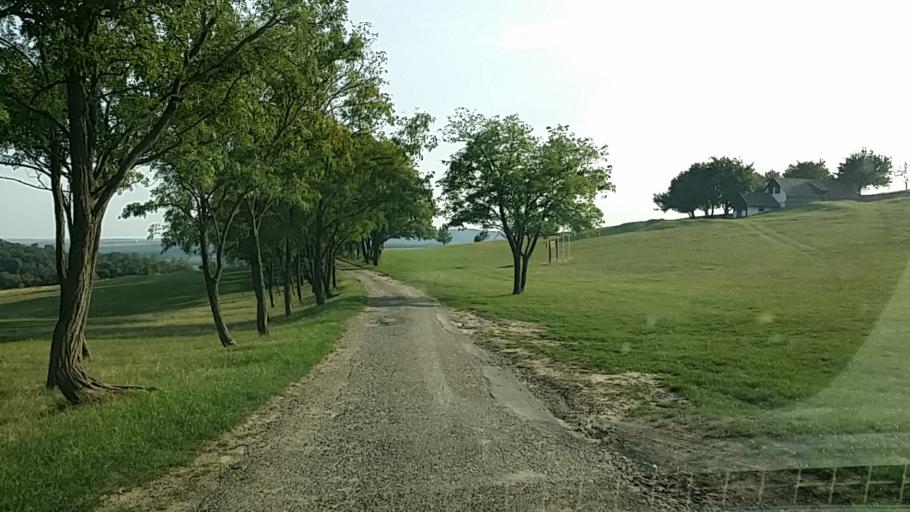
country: HU
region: Nograd
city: Bujak
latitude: 47.8780
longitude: 19.5004
